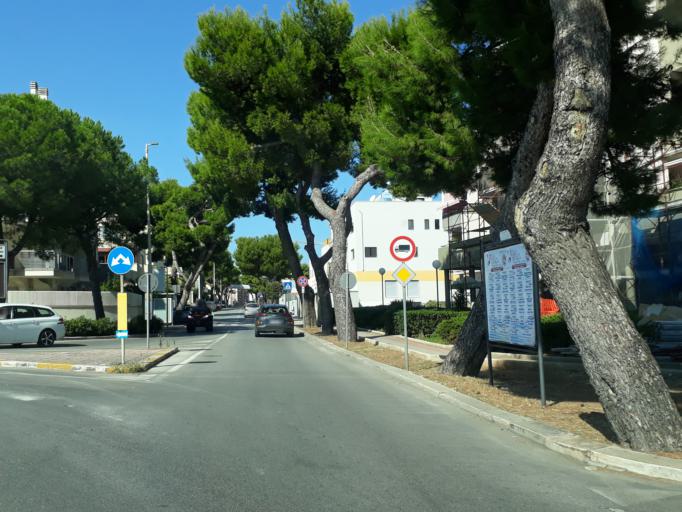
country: IT
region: Apulia
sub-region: Provincia di Bari
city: Monopoli
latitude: 40.9429
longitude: 17.3037
